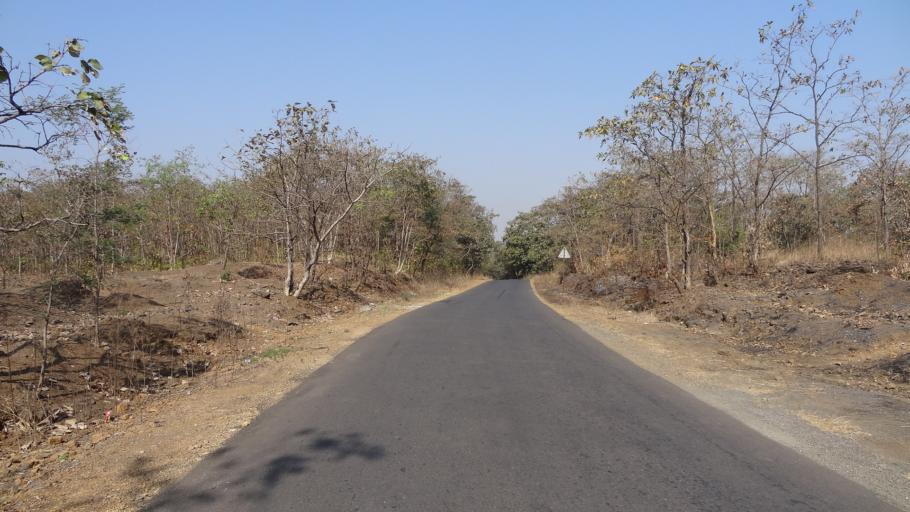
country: IN
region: Maharashtra
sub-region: Thane
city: Murbad
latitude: 19.2987
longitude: 73.3977
